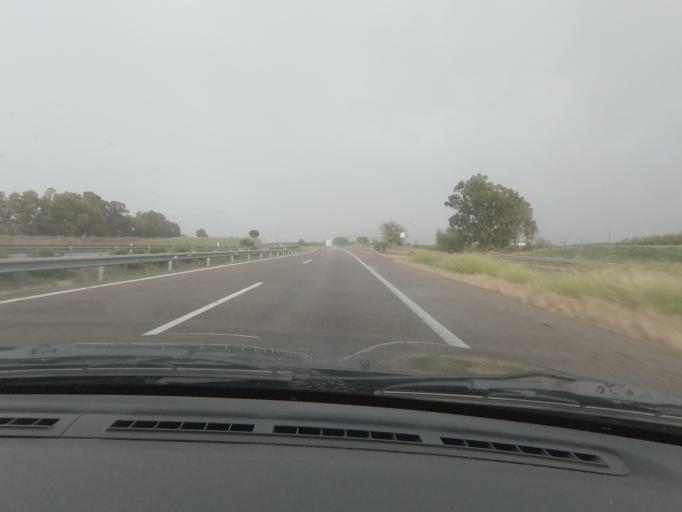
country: ES
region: Extremadura
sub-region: Provincia de Badajoz
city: Arroyo de San Servan
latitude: 38.8672
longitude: -6.5020
